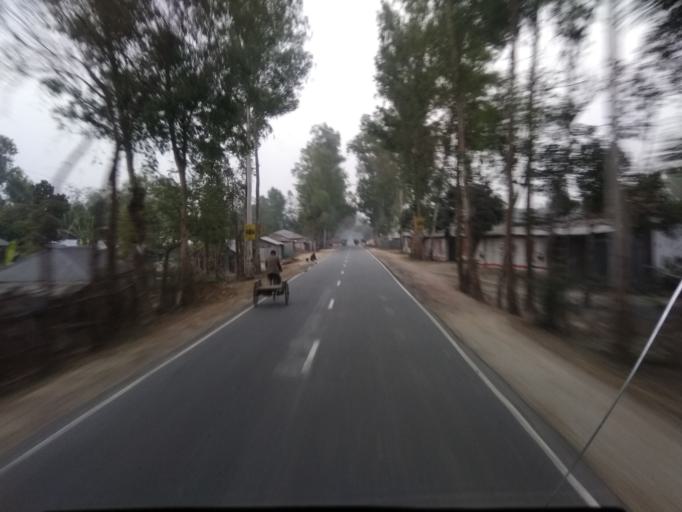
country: BD
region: Rajshahi
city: Bogra
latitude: 24.6763
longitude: 89.2832
